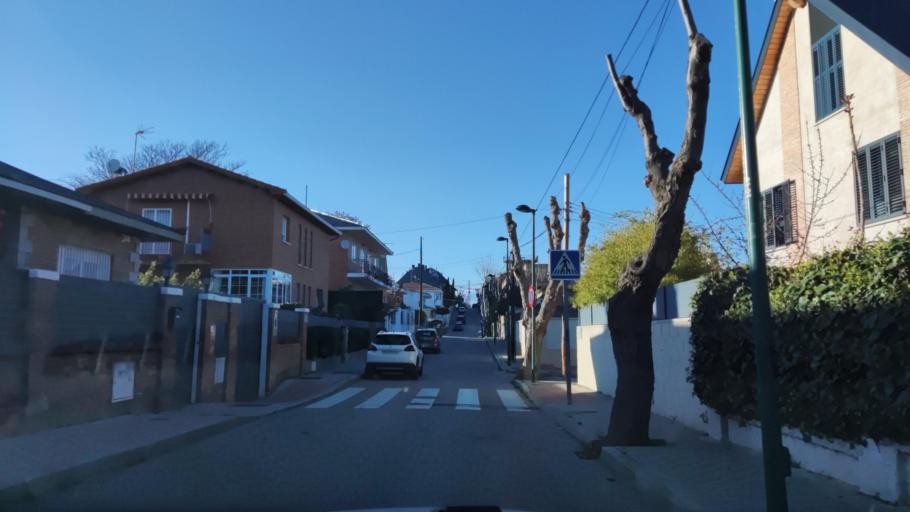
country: ES
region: Madrid
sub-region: Provincia de Madrid
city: Latina
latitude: 40.4050
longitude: -3.7791
